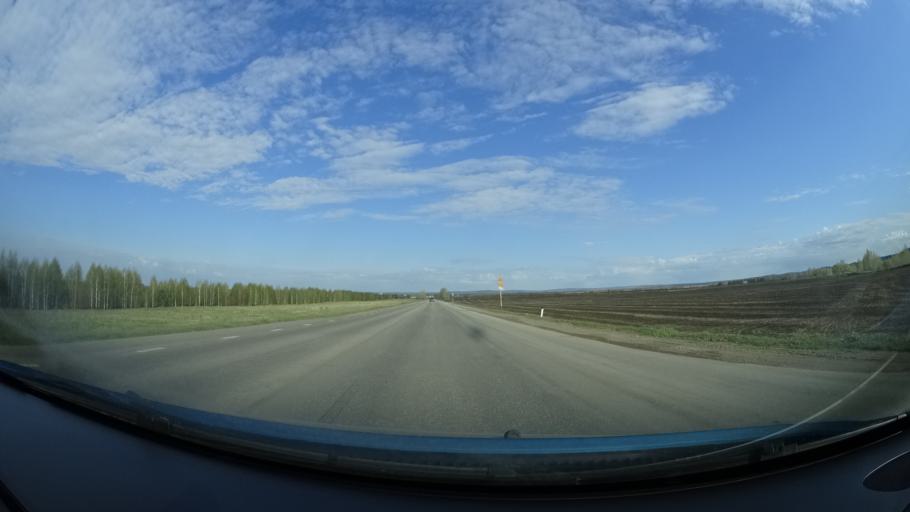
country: RU
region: Bashkortostan
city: Blagoveshchensk
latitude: 55.1868
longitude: 55.8464
